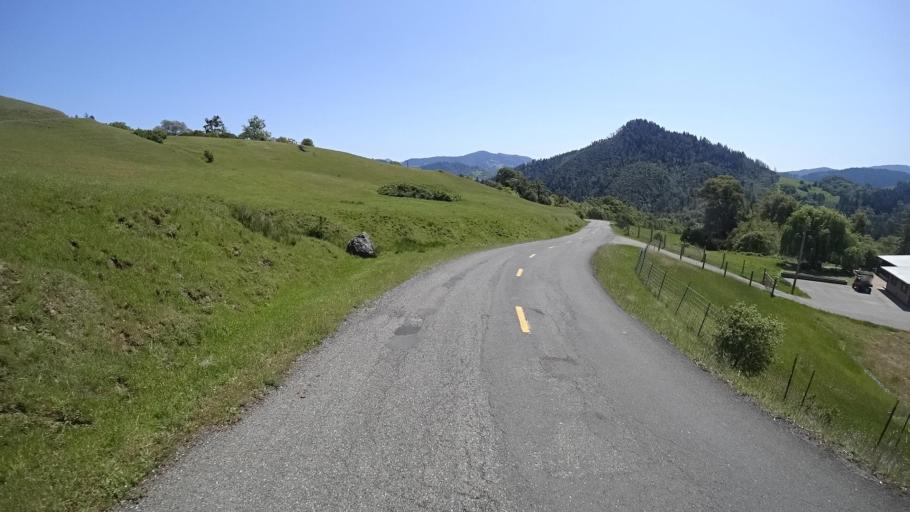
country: US
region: California
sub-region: Humboldt County
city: Redway
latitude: 40.2381
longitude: -123.6220
